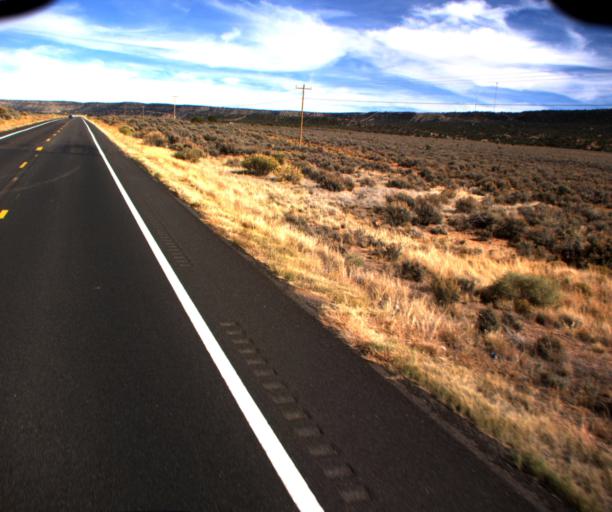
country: US
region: Arizona
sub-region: Navajo County
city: Kayenta
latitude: 36.5488
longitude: -110.5310
